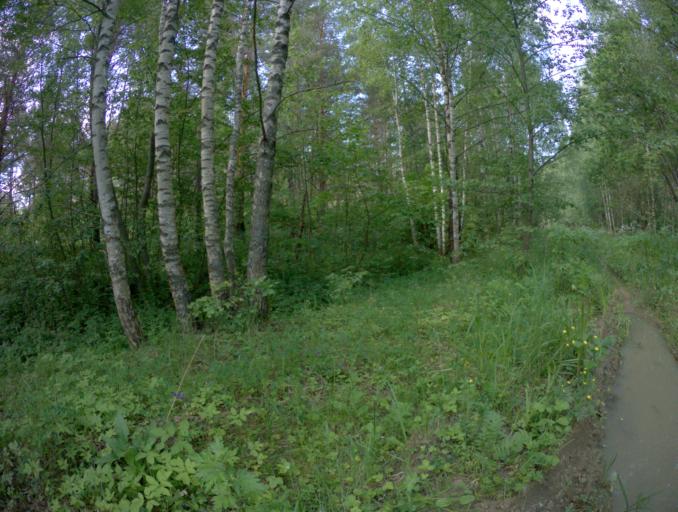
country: RU
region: Vladimir
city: Stavrovo
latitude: 56.3184
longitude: 39.9529
